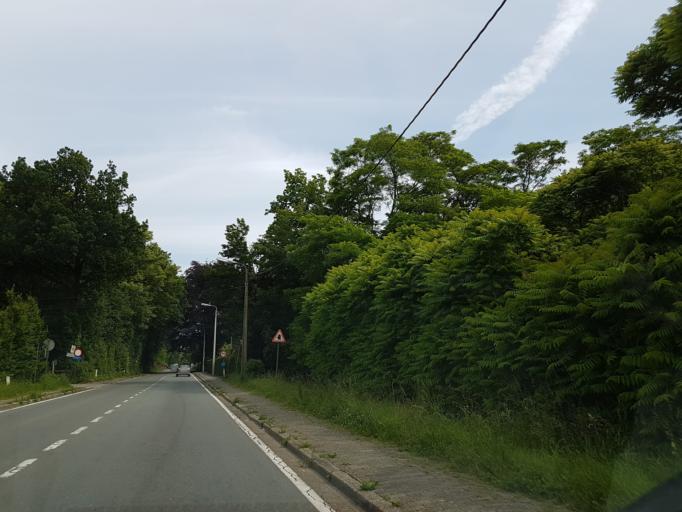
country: BE
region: Flanders
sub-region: Provincie Vlaams-Brabant
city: Ternat
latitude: 50.8883
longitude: 4.1695
